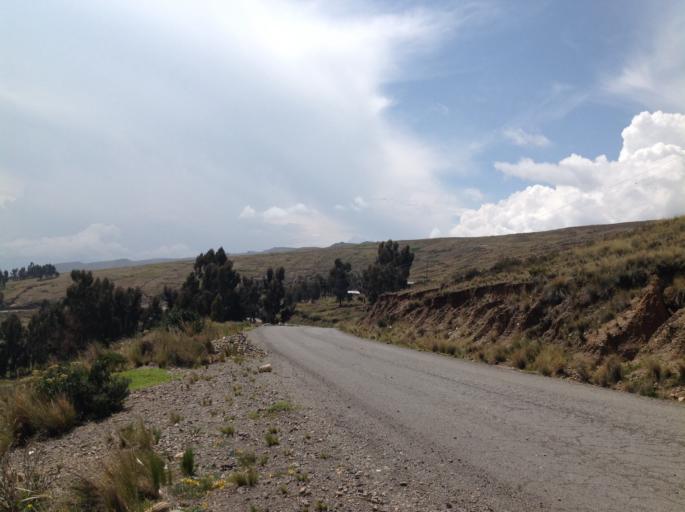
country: BO
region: La Paz
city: Yumani
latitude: -15.8579
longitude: -68.9778
